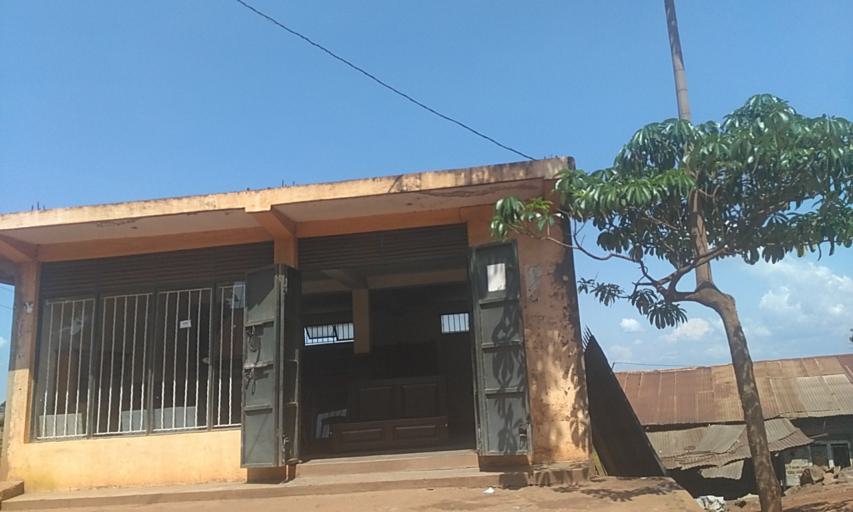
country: UG
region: Central Region
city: Kampala Central Division
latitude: 0.3806
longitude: 32.5976
